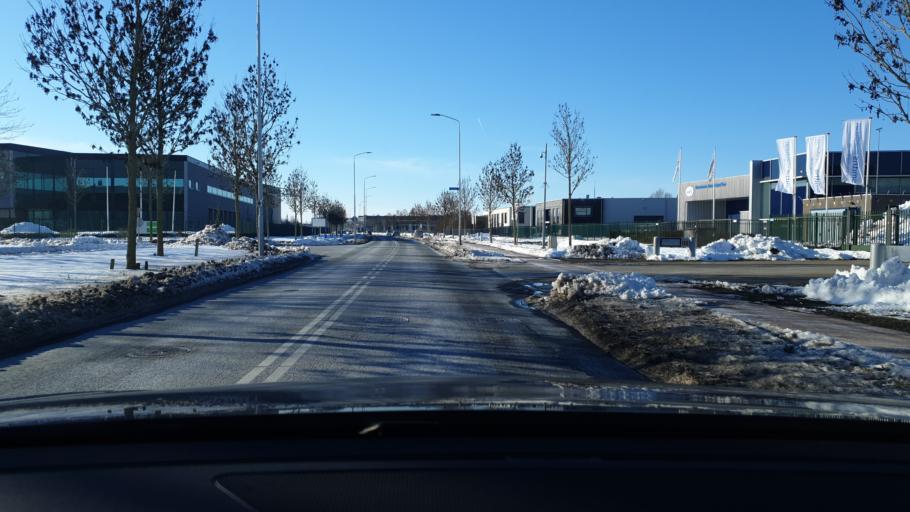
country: NL
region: Gelderland
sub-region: Gemeente Beuningen
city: Beuningen
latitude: 51.8301
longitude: 5.7565
